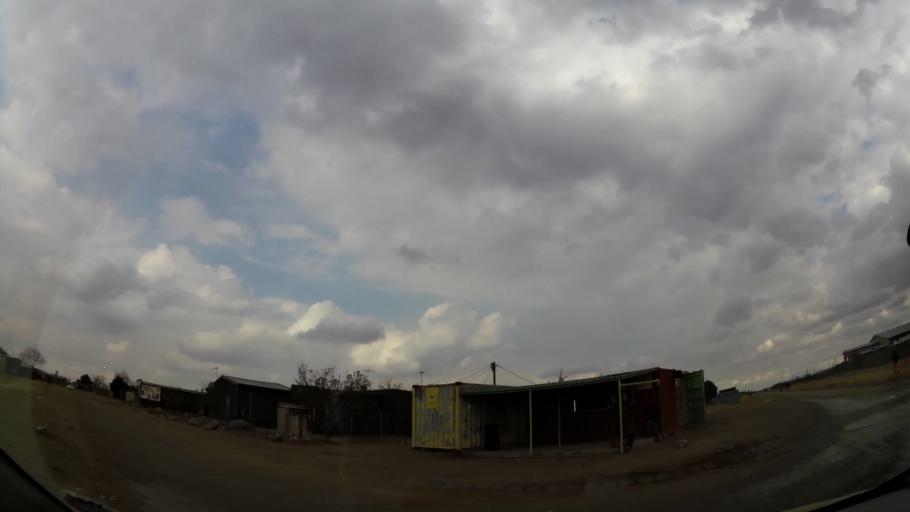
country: ZA
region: Orange Free State
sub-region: Fezile Dabi District Municipality
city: Sasolburg
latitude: -26.8625
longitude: 27.8747
